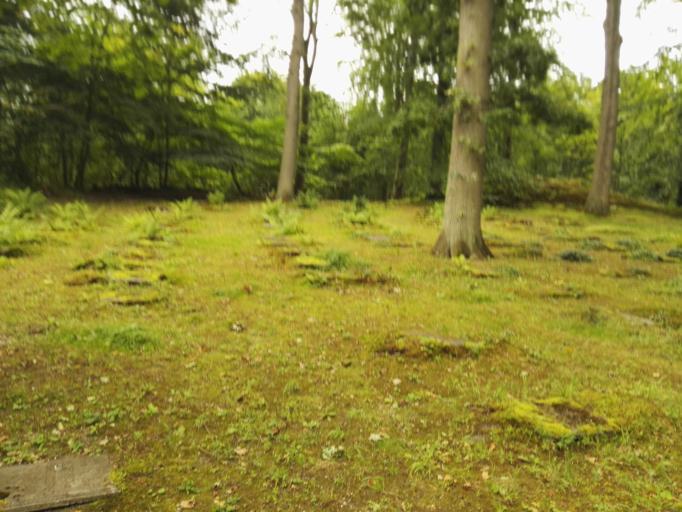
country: DK
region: Zealand
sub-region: Odsherred Kommune
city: Nykobing Sjaelland
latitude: 55.9126
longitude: 11.6596
